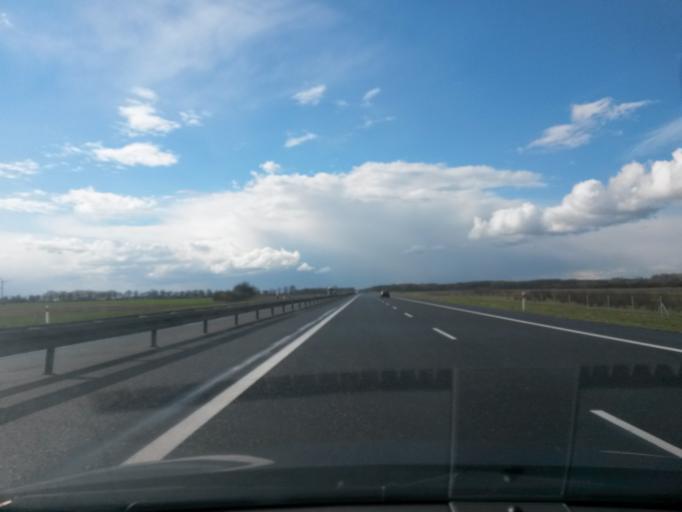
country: PL
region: Greater Poland Voivodeship
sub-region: Powiat wrzesinski
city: Wrzesnia
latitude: 52.2986
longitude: 17.6347
